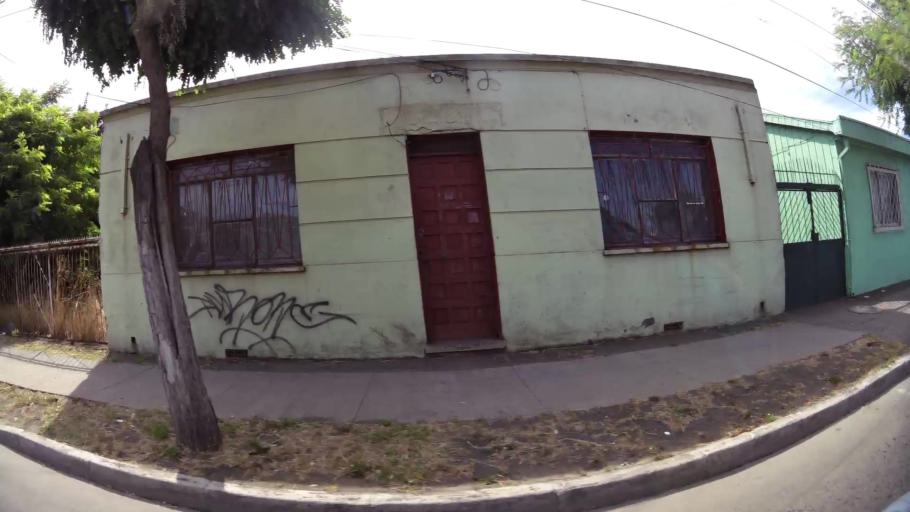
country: CL
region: Biobio
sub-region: Provincia de Concepcion
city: Talcahuano
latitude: -36.7206
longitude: -73.1183
